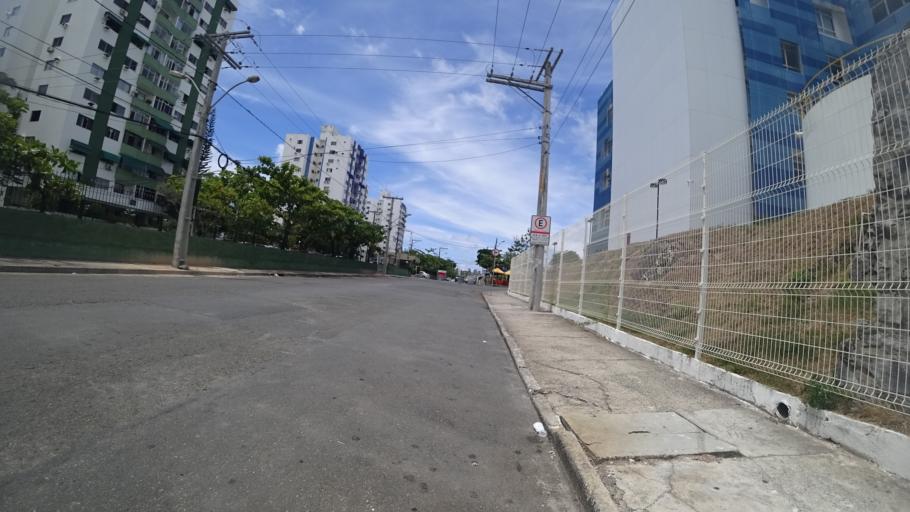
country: BR
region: Bahia
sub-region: Salvador
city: Salvador
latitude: -12.9657
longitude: -38.4354
